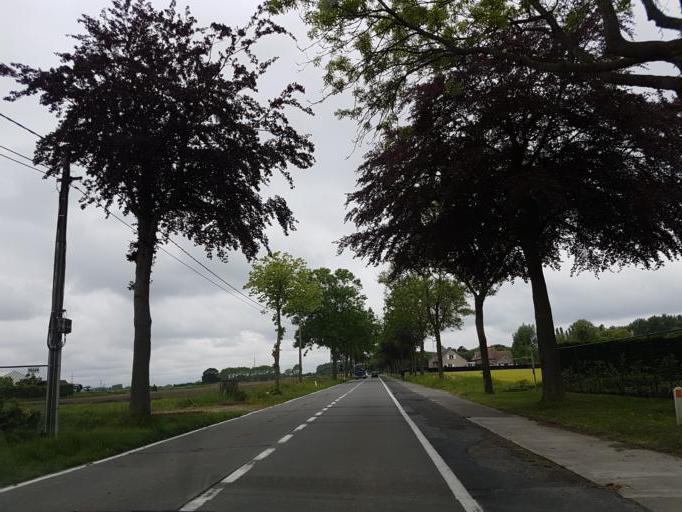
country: BE
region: Flanders
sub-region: Provincie Oost-Vlaanderen
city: Zomergem
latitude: 51.1154
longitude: 3.5386
